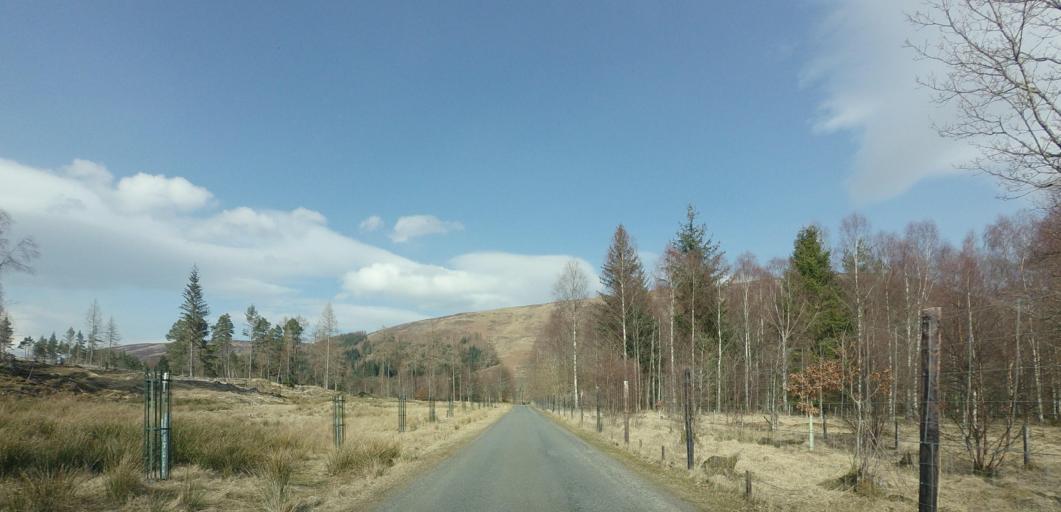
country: GB
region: Scotland
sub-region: Stirling
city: Callander
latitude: 56.5966
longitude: -4.3036
